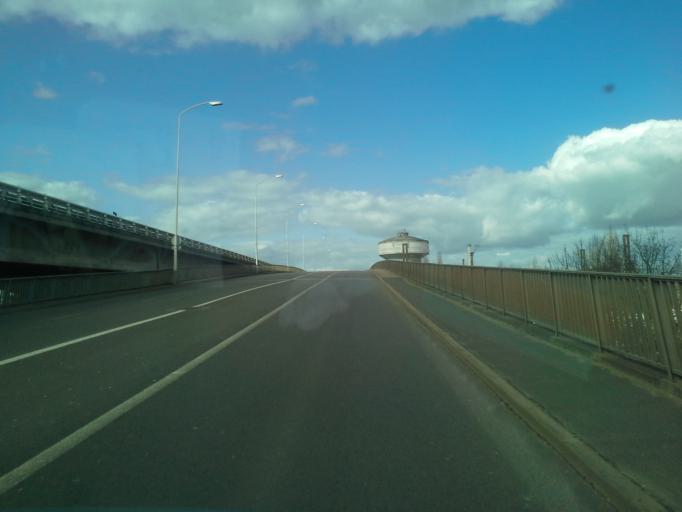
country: FR
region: Centre
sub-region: Departement d'Indre-et-Loire
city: Tours
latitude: 47.3804
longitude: 0.7130
